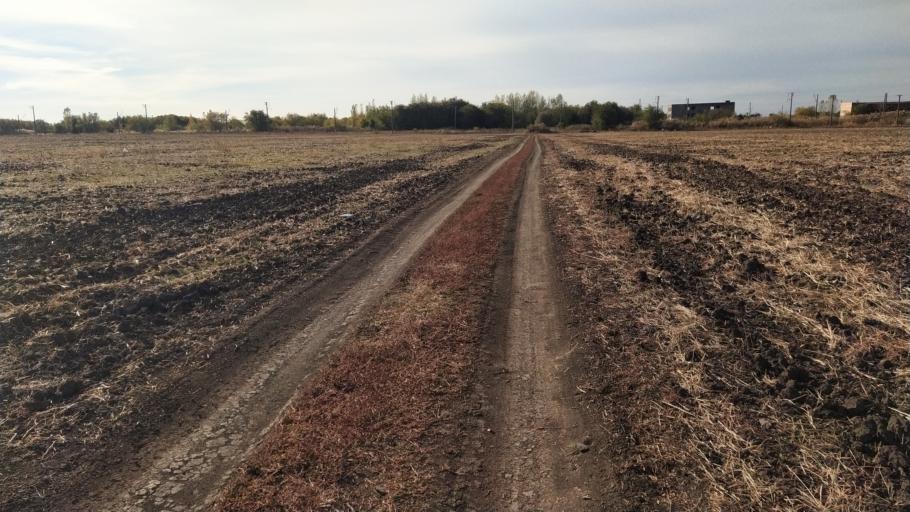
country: RU
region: Rostov
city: Bataysk
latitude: 47.1141
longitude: 39.7172
